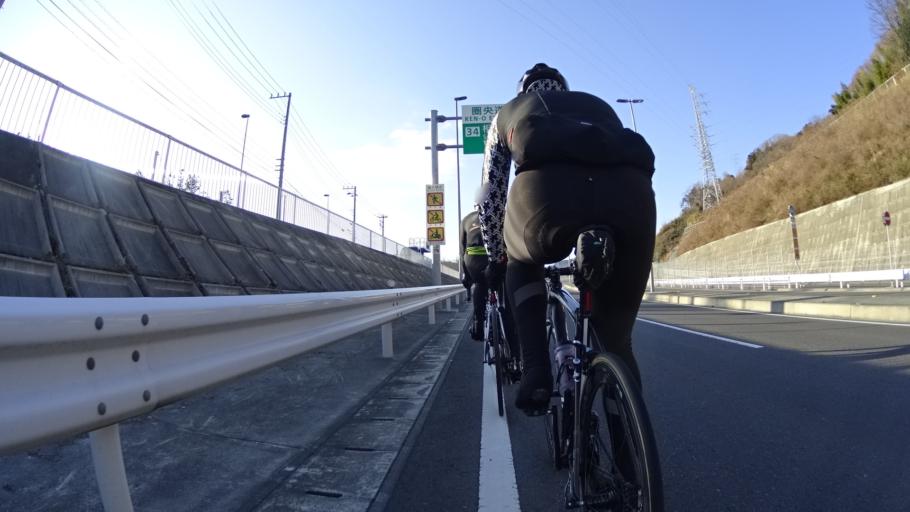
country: JP
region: Tokyo
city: Hachioji
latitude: 35.5824
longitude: 139.2904
